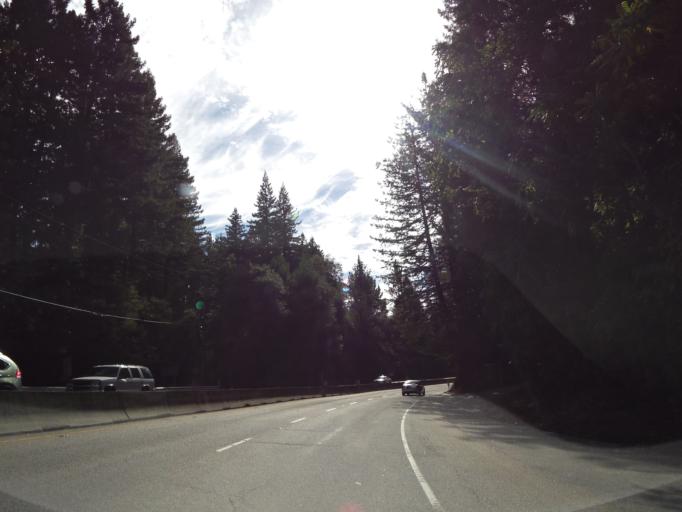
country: US
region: California
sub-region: Santa Cruz County
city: Scotts Valley
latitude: 37.0982
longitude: -121.9753
